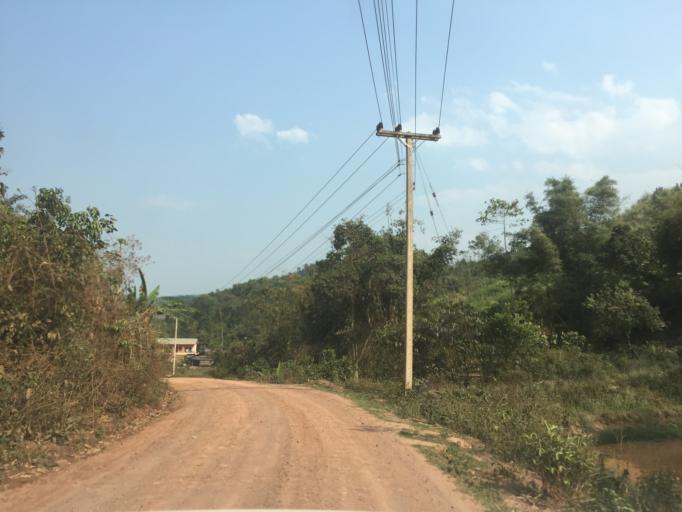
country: LA
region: Oudomxai
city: Muang La
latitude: 21.0742
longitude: 101.8212
